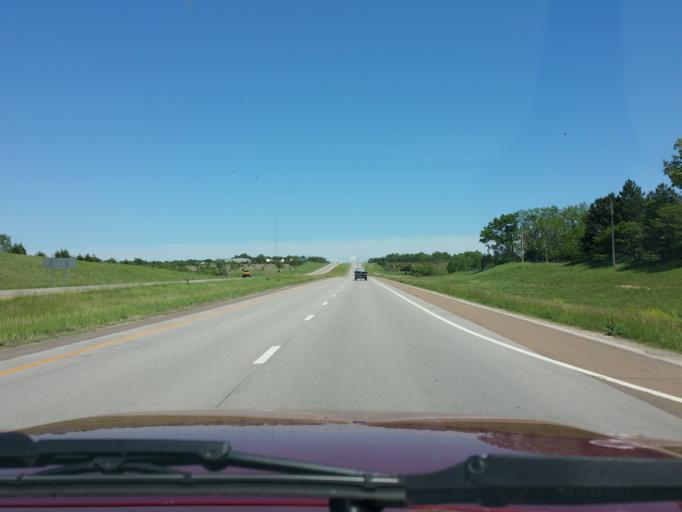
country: US
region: Kansas
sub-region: Pottawatomie County
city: Wamego
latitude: 39.2103
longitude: -96.3634
